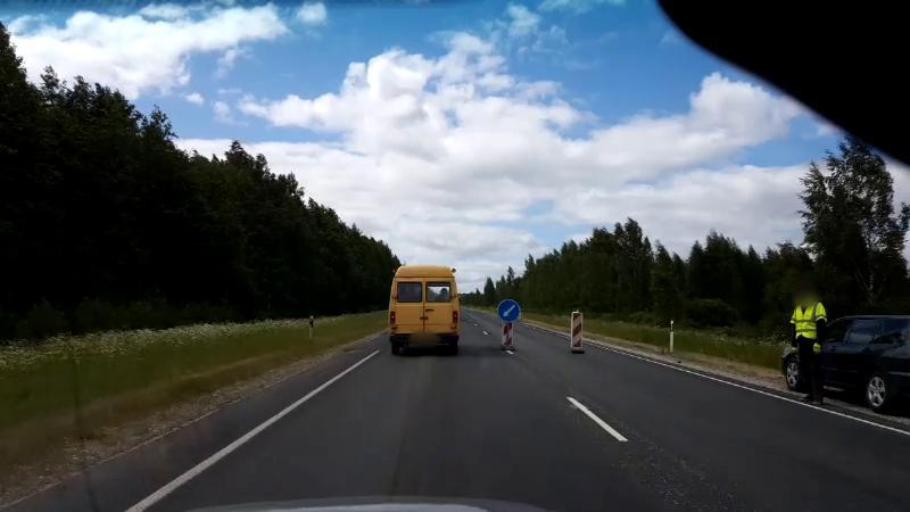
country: LV
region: Salacgrivas
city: Ainazi
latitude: 58.0031
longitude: 24.4828
